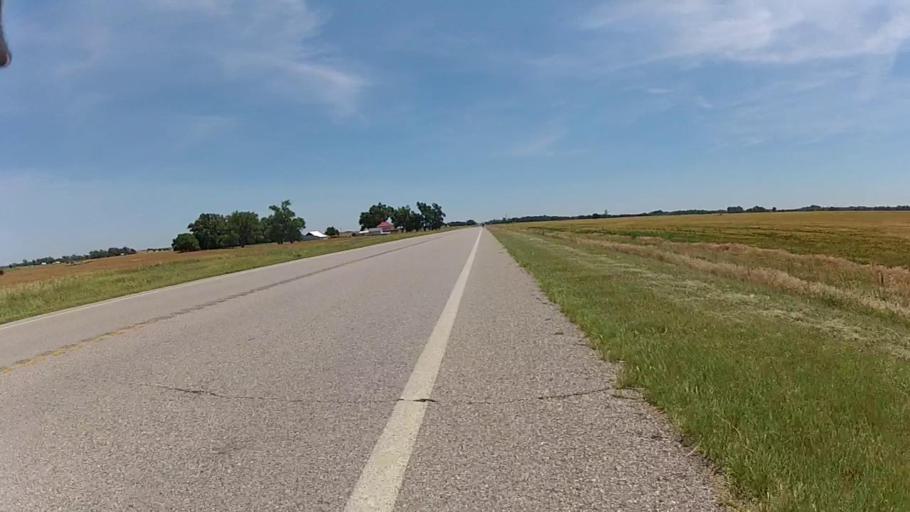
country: US
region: Kansas
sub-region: Barber County
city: Medicine Lodge
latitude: 37.2534
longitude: -98.4489
